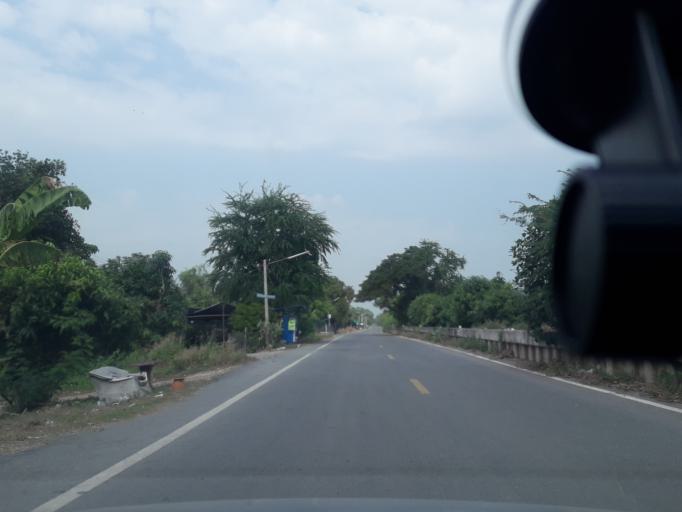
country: TH
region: Sara Buri
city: Nong Khae
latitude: 14.2494
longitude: 100.8913
